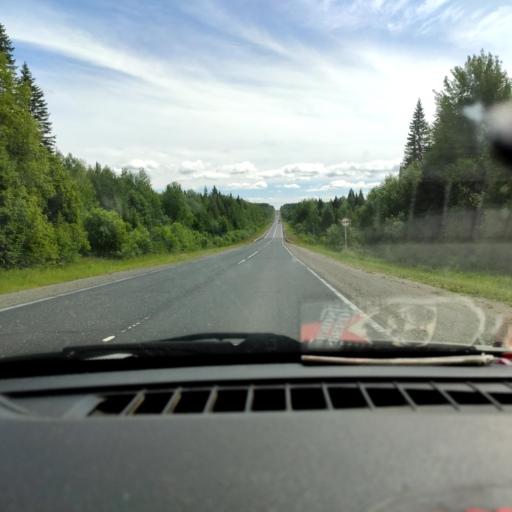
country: RU
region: Perm
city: Chusovoy
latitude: 58.3739
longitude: 57.9739
